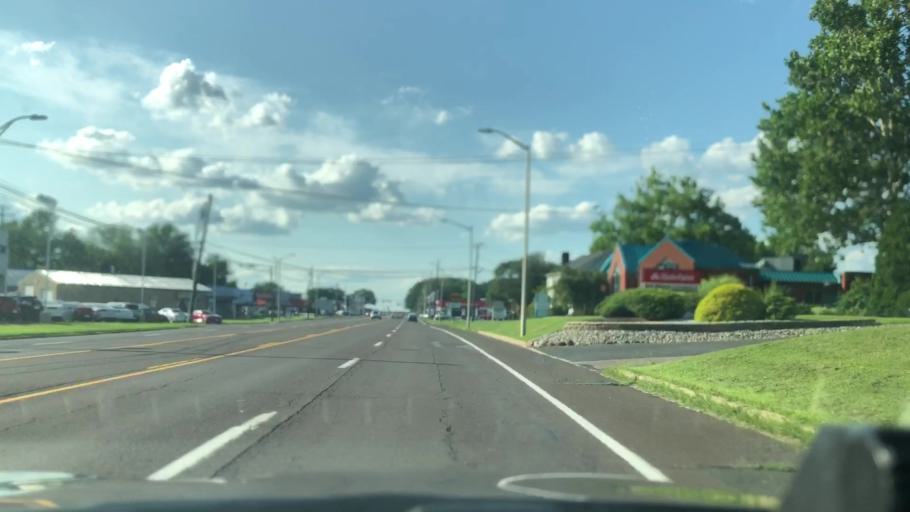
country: US
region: Pennsylvania
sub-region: Bucks County
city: Quakertown
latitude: 40.4331
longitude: -75.3517
